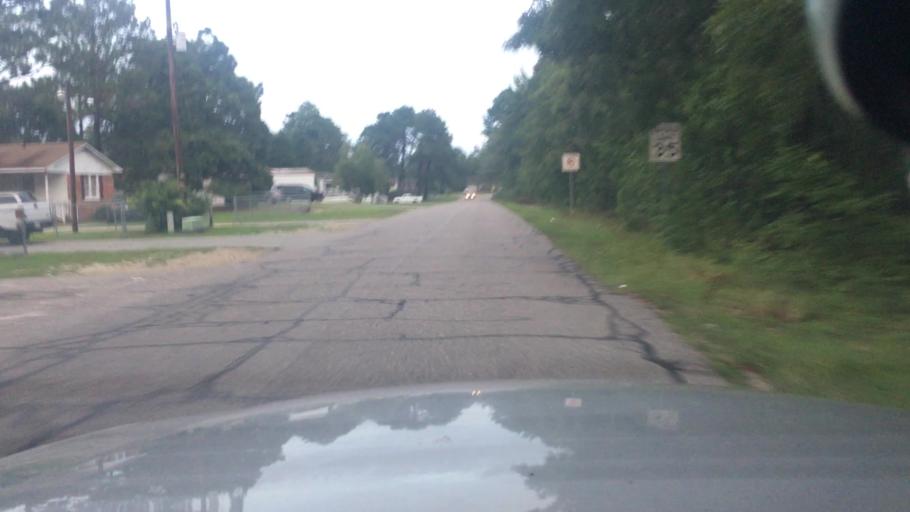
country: US
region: North Carolina
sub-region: Cumberland County
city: Hope Mills
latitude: 34.9863
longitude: -78.9254
